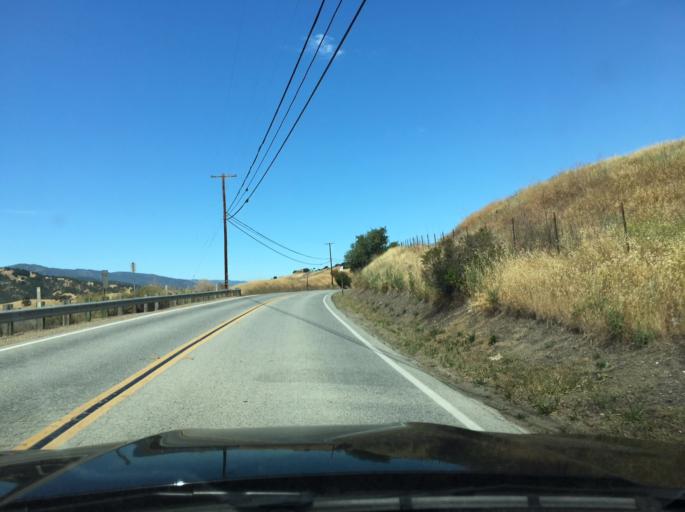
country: US
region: California
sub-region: Santa Clara County
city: Seven Trees
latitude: 37.1858
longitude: -121.7699
